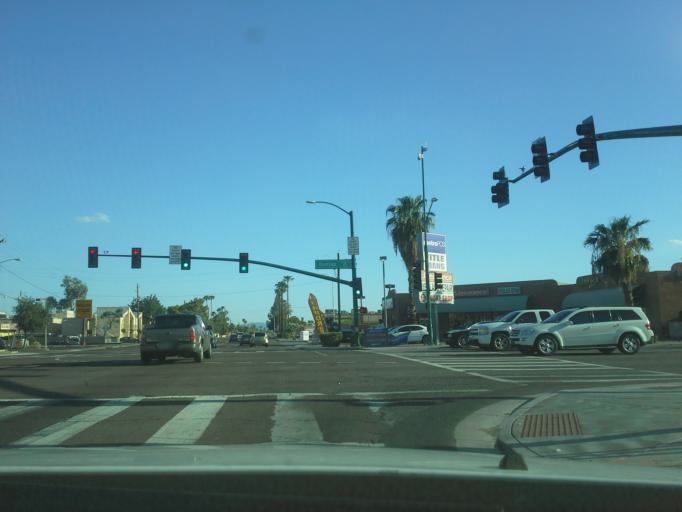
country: US
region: Arizona
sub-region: Maricopa County
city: Glendale
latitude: 33.5678
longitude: -112.1344
